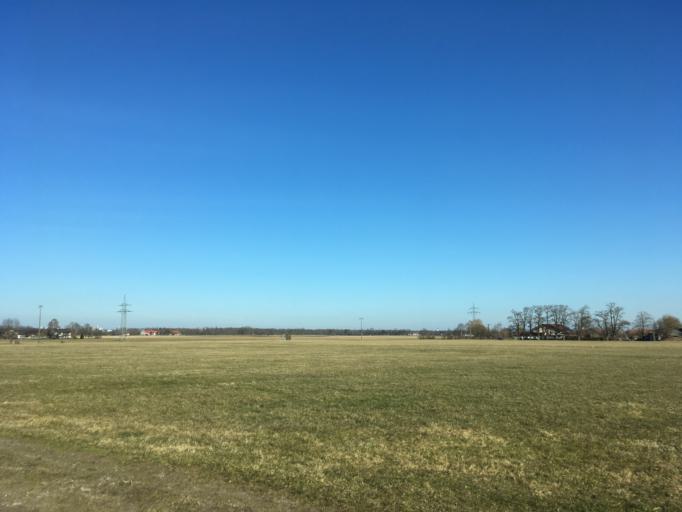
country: DE
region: Bavaria
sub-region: Upper Bavaria
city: Irschenberg
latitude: 47.8552
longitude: 11.9451
